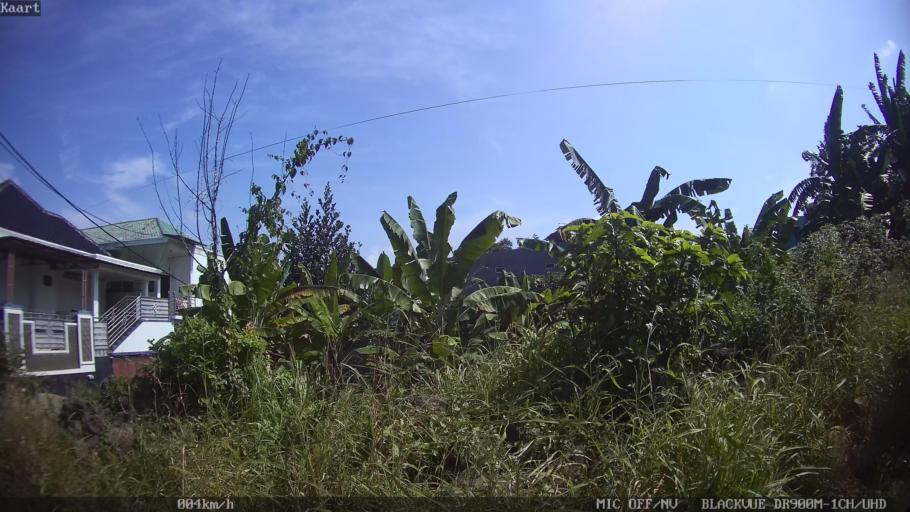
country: ID
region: Lampung
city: Kedaton
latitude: -5.3713
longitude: 105.2441
